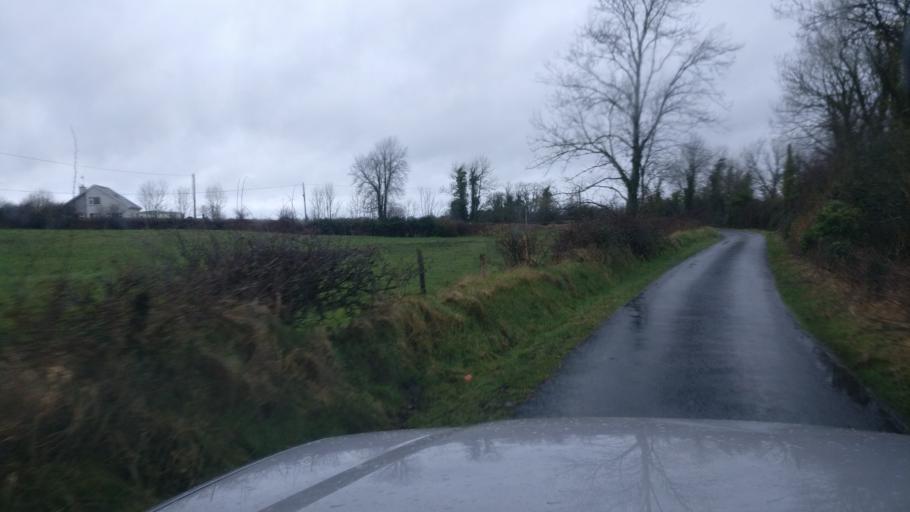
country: IE
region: Connaught
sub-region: County Galway
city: Ballinasloe
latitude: 53.2469
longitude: -8.3540
